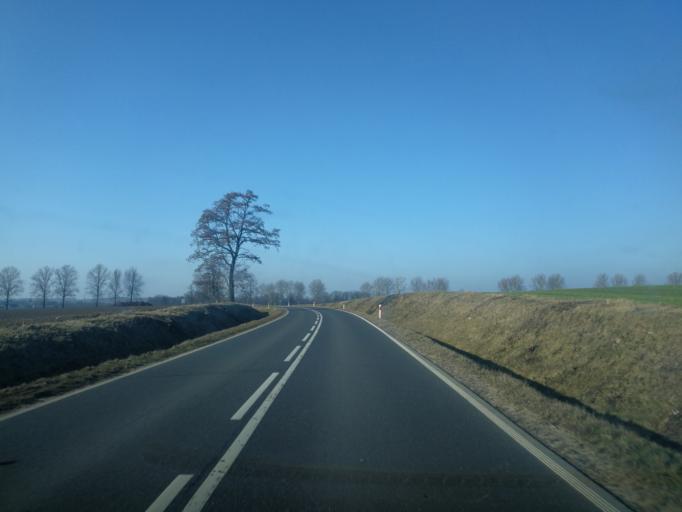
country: PL
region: Warmian-Masurian Voivodeship
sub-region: Powiat ilawski
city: Lubawa
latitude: 53.4169
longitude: 19.7896
